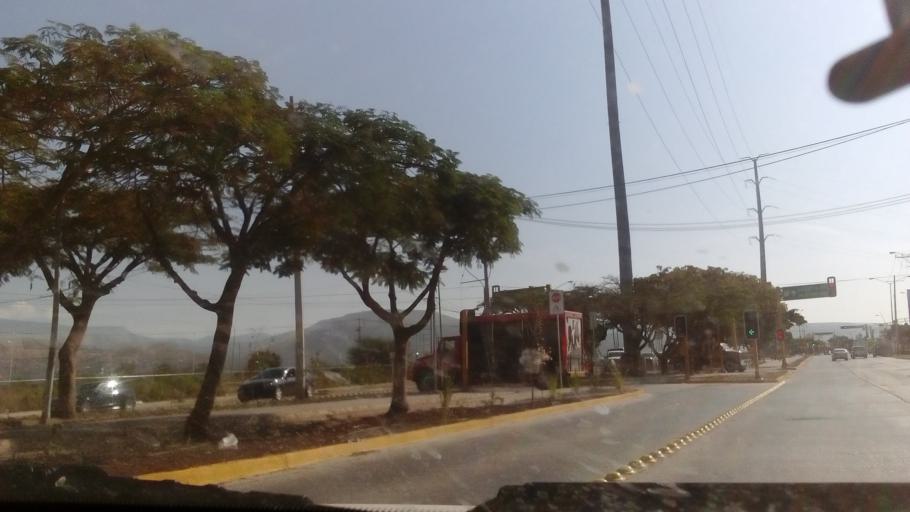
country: MX
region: Guanajuato
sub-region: Leon
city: Medina
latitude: 21.1419
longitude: -101.6348
